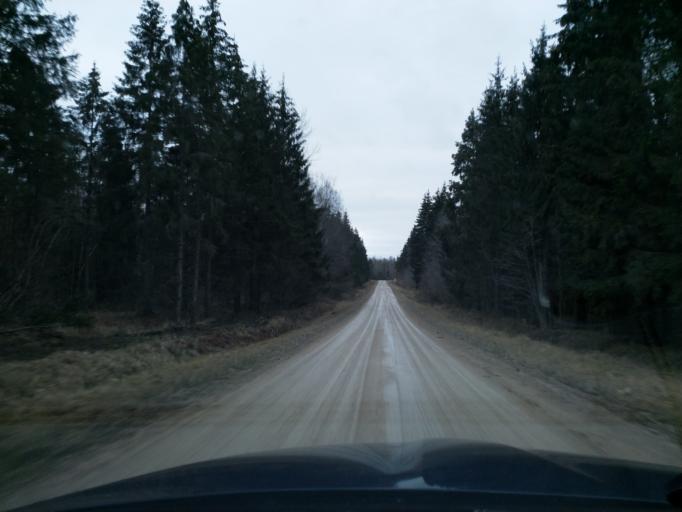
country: LV
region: Kuldigas Rajons
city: Kuldiga
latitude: 56.9031
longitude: 22.2581
